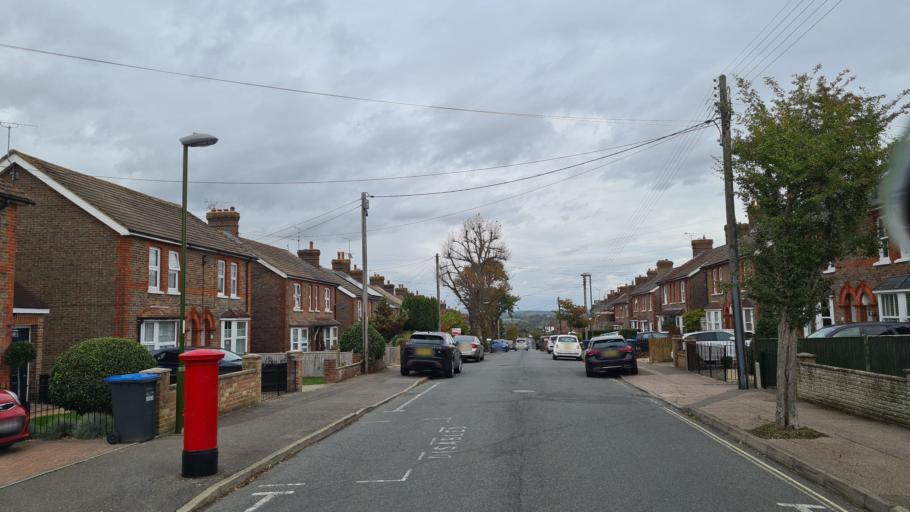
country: GB
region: England
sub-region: West Sussex
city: Haywards Heath
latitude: 50.9941
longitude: -0.0962
